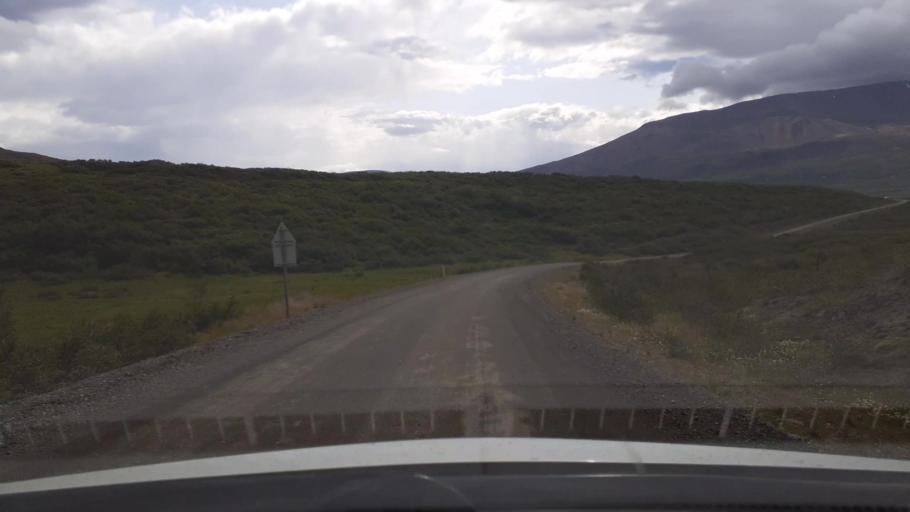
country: IS
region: West
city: Borgarnes
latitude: 64.5580
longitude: -21.6251
